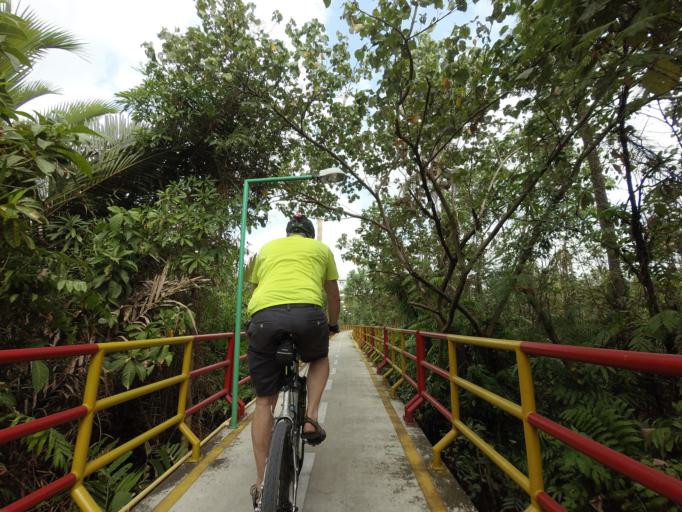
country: TH
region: Samut Prakan
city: Phra Pradaeng
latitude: 13.6624
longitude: 100.5649
